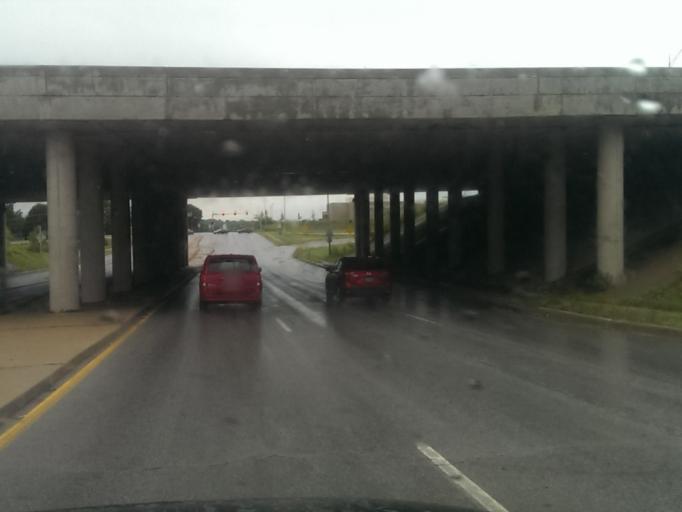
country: US
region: Kansas
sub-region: Johnson County
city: Leawood
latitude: 38.9399
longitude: -94.5830
